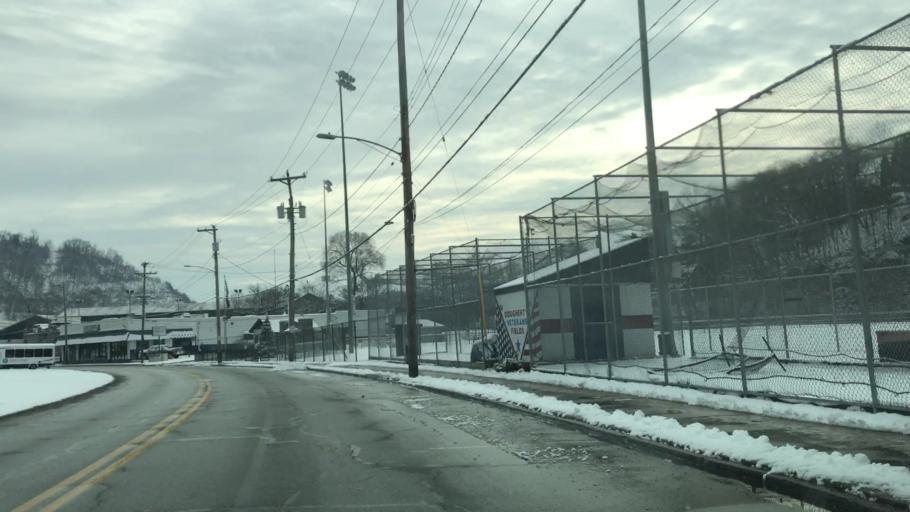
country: US
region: Pennsylvania
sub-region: Allegheny County
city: Etna
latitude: 40.5026
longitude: -79.9479
